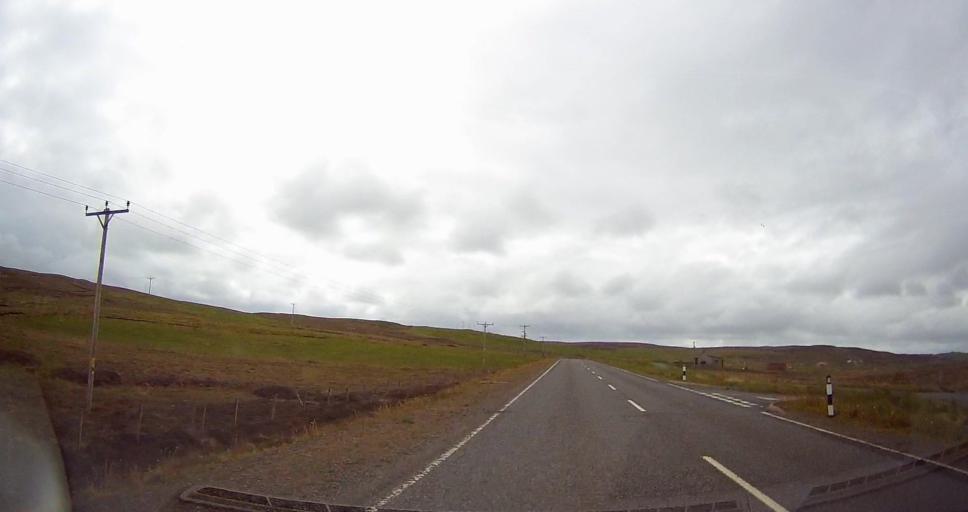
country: GB
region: Scotland
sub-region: Shetland Islands
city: Lerwick
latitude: 60.2563
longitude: -1.4452
